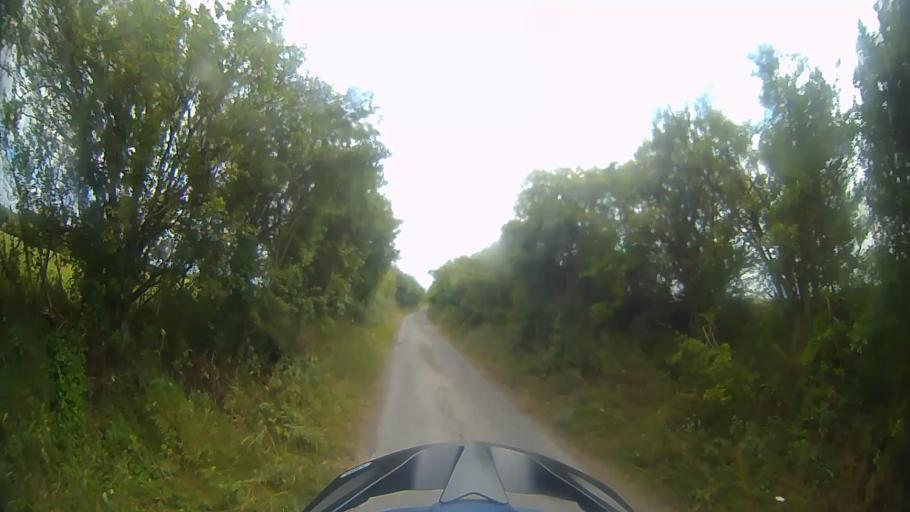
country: GB
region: England
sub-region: Oxfordshire
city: Wantage
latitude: 51.5627
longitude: -1.4460
